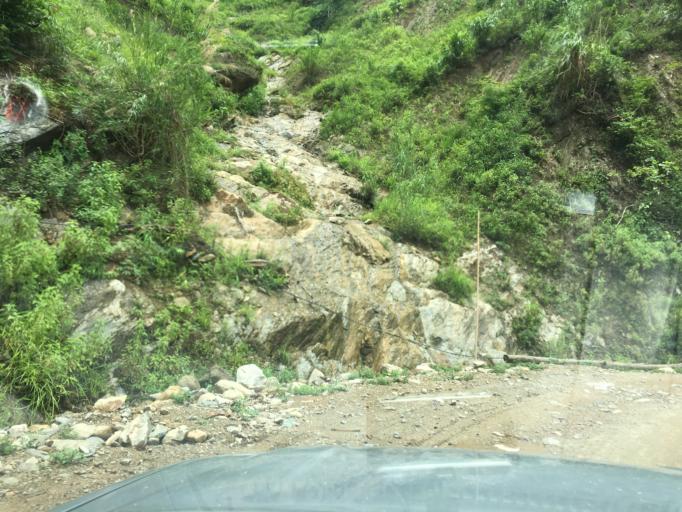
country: VN
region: Yen Bai
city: Son Thinh
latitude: 21.6782
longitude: 104.5546
